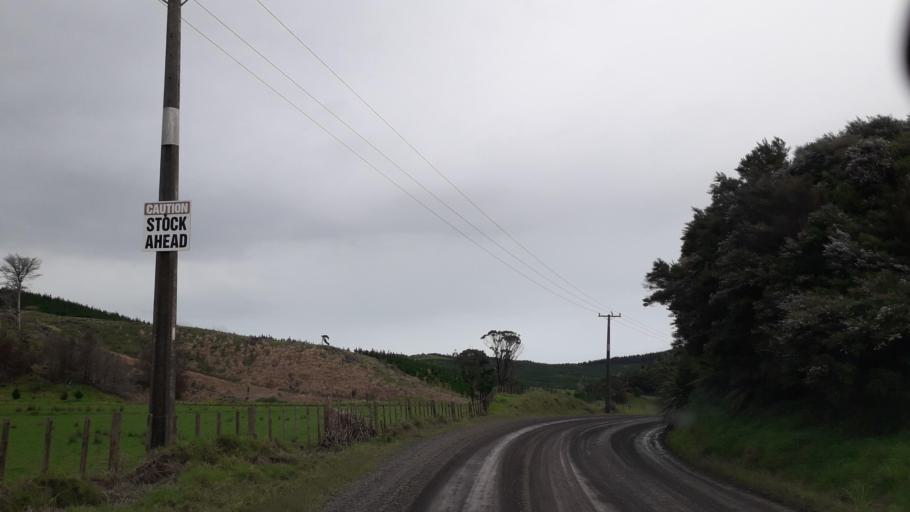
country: NZ
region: Northland
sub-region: Far North District
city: Ahipara
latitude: -35.4300
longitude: 173.3511
